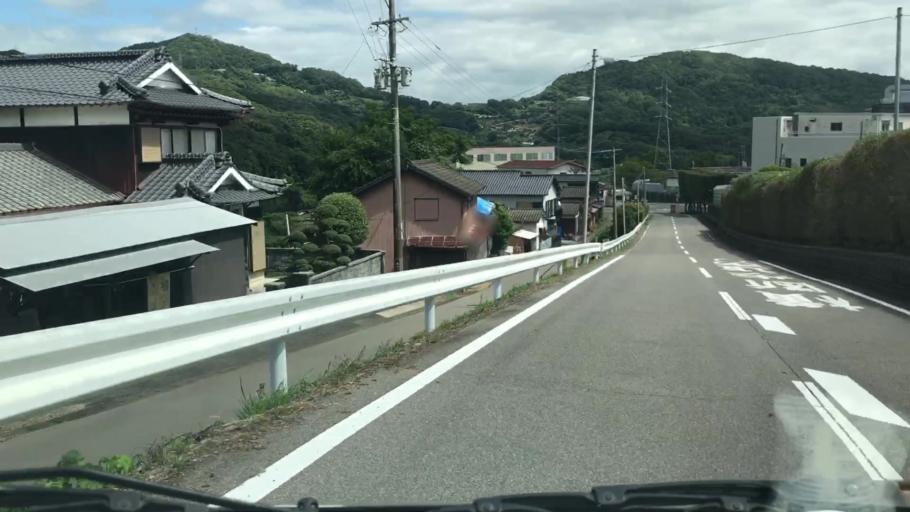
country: JP
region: Saga Prefecture
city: Takeocho-takeo
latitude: 33.2324
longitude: 130.1397
